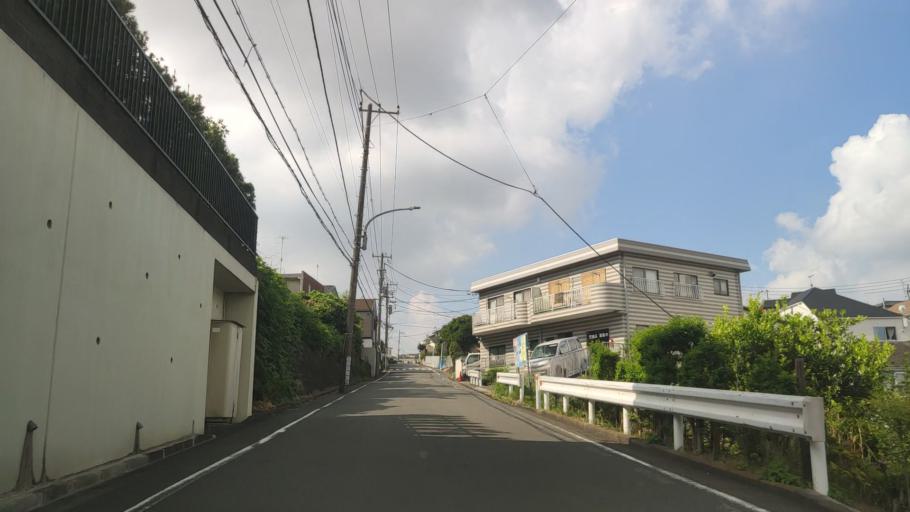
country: JP
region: Kanagawa
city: Yokohama
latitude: 35.4023
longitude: 139.5651
